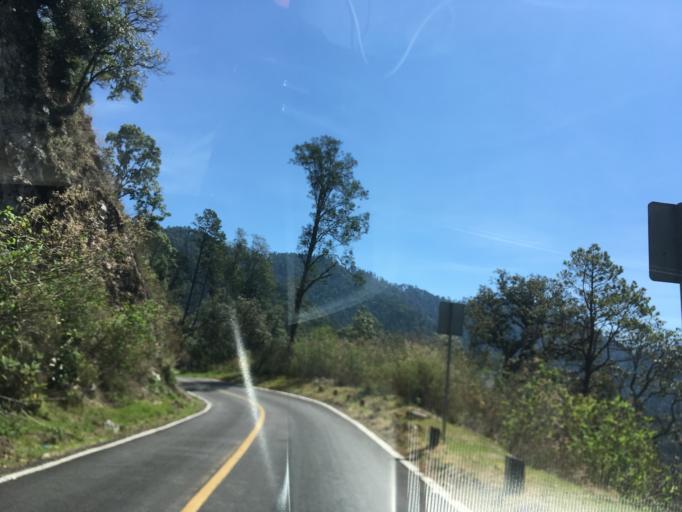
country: MX
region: Michoacan
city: Tzitzio
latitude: 19.6649
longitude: -100.8105
